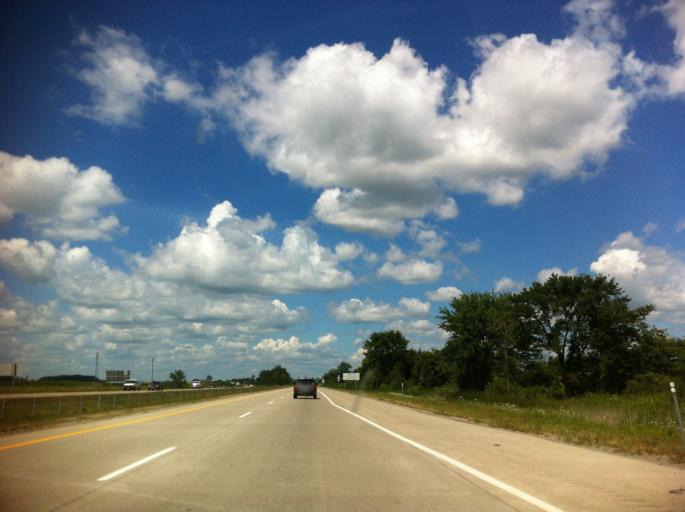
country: US
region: Ohio
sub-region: Lucas County
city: Sylvania
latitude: 41.7739
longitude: -83.6950
